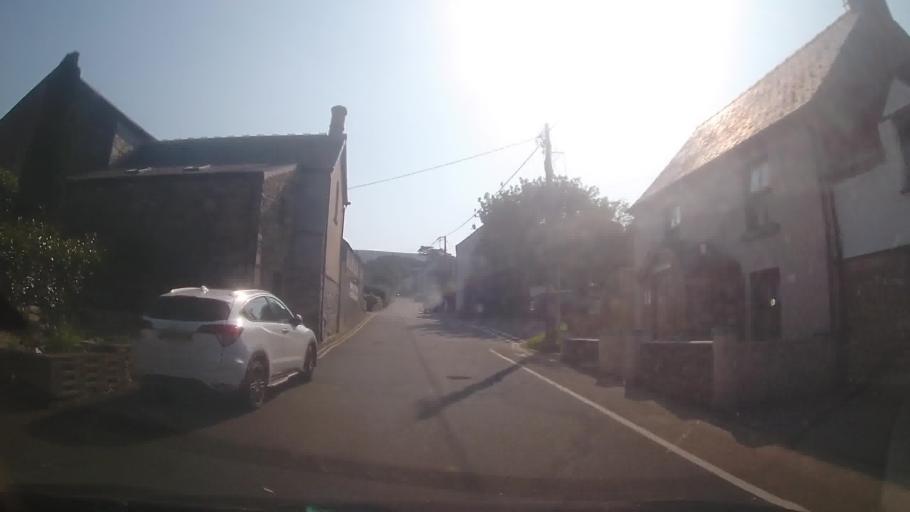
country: GB
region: Wales
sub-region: Pembrokeshire
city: Newport
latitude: 52.0176
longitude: -4.8326
